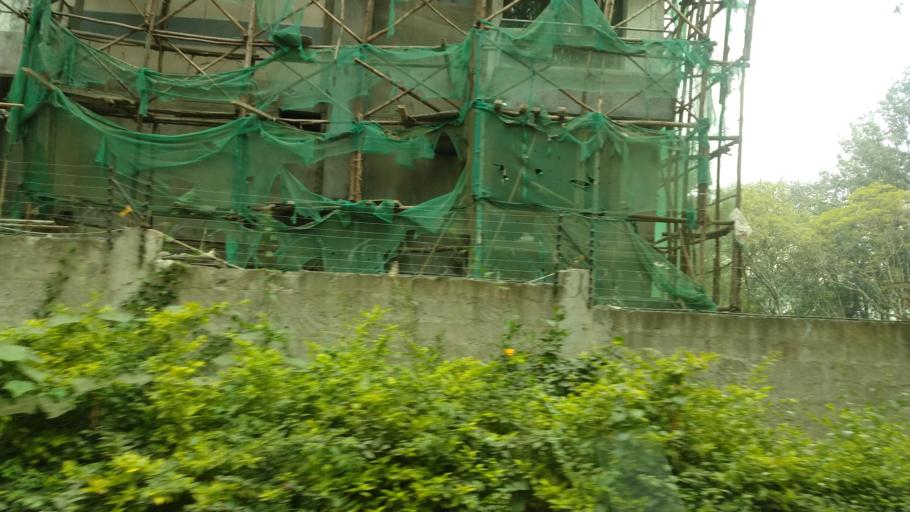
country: KE
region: Nairobi Area
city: Nairobi
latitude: -1.2950
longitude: 36.7766
